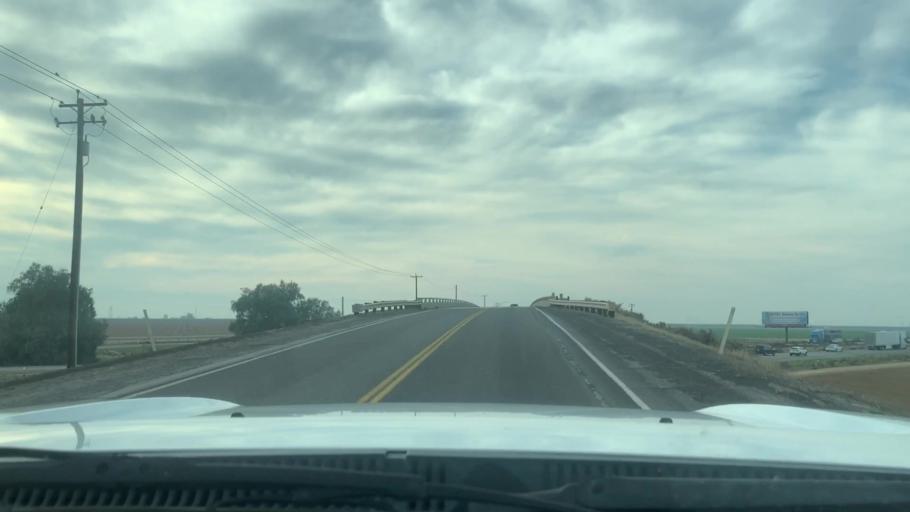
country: US
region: California
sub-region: Kern County
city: Buttonwillow
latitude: 35.4423
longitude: -119.4556
